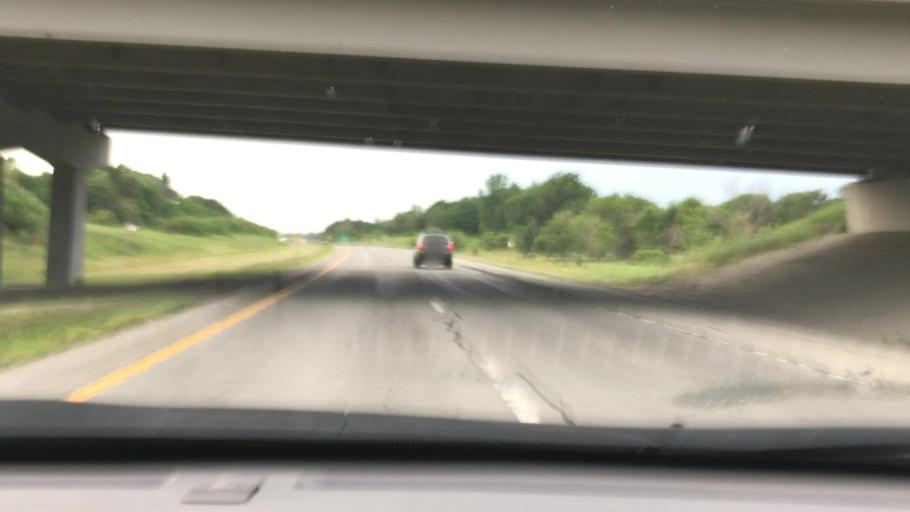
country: US
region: New York
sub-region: Erie County
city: Orchard Park
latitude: 42.7490
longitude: -78.7606
